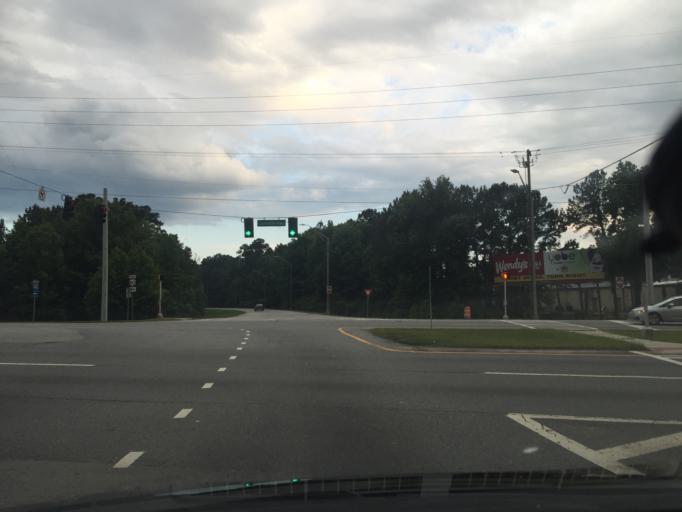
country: US
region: Georgia
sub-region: Chatham County
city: Pooler
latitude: 32.1131
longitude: -81.2391
